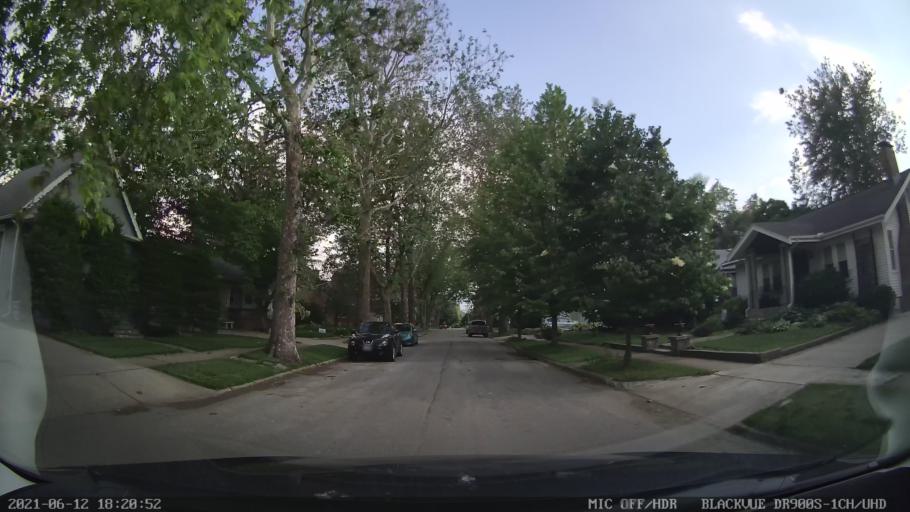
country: US
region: Illinois
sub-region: McLean County
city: Bloomington
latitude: 40.4771
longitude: -88.9709
